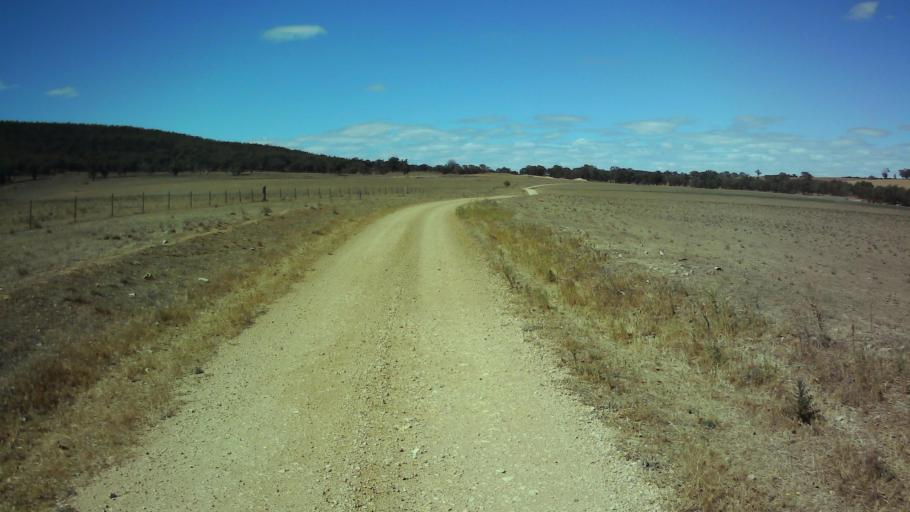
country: AU
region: New South Wales
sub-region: Weddin
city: Grenfell
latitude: -34.0374
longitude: 148.4333
